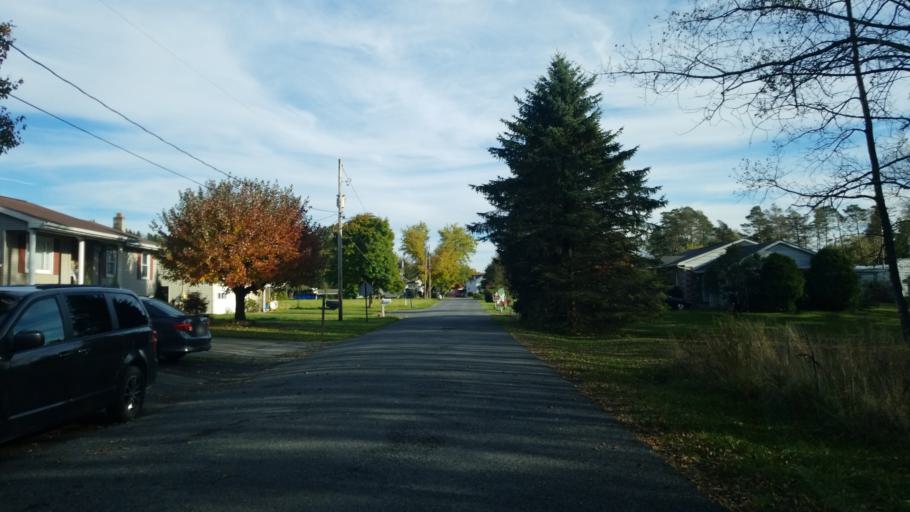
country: US
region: Pennsylvania
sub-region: Jefferson County
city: Brockway
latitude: 41.2495
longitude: -78.7874
